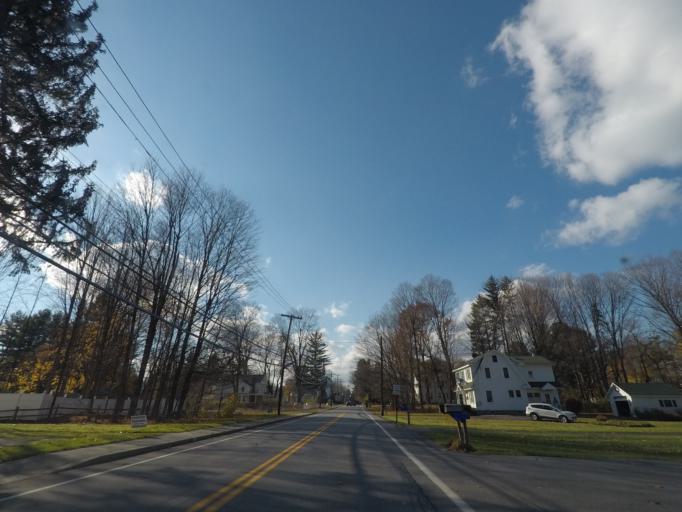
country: US
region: New York
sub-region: Schenectady County
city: East Glenville
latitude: 42.9103
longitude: -73.8888
